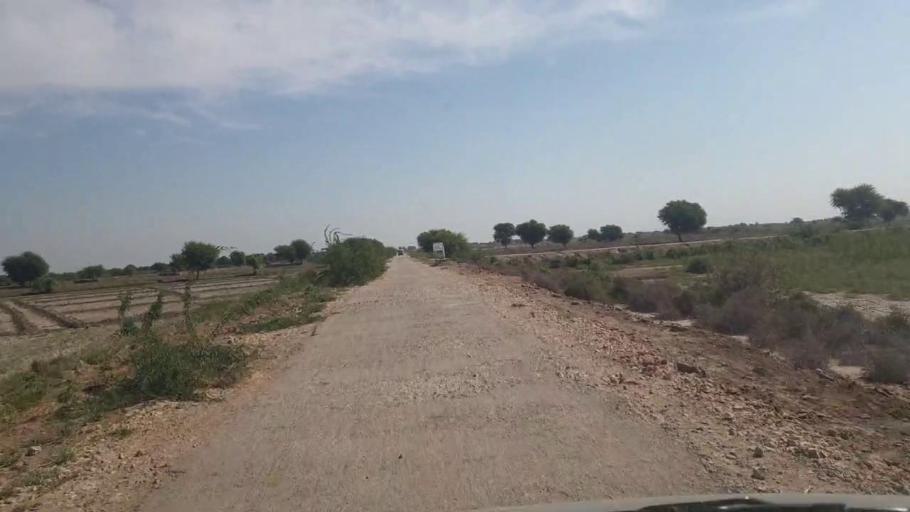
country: PK
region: Sindh
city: Tando Bago
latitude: 24.9439
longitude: 69.0915
